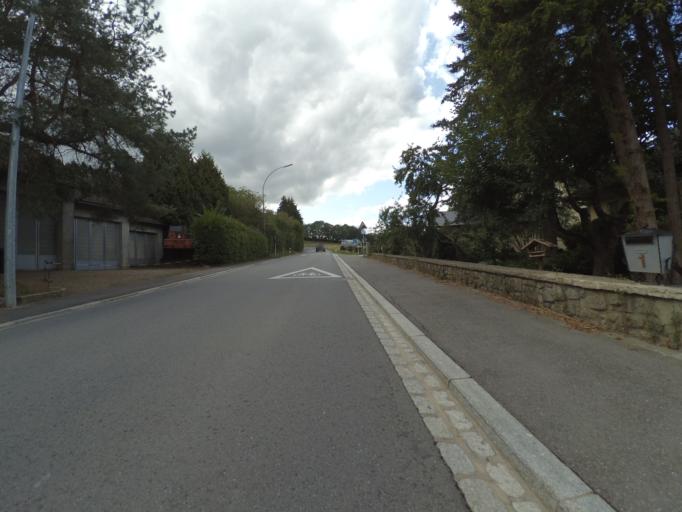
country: LU
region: Grevenmacher
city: Gonderange
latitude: 49.6771
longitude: 6.2453
